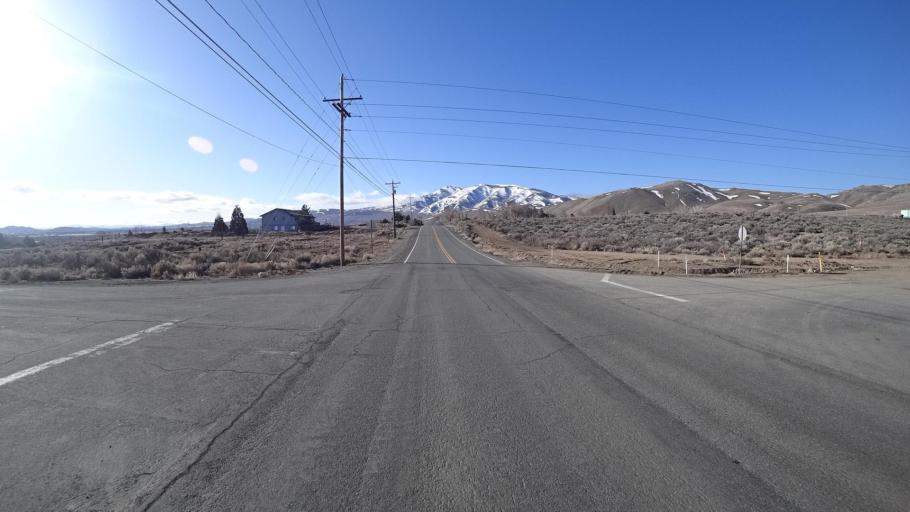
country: US
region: Nevada
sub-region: Washoe County
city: Cold Springs
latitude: 39.6675
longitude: -119.9224
